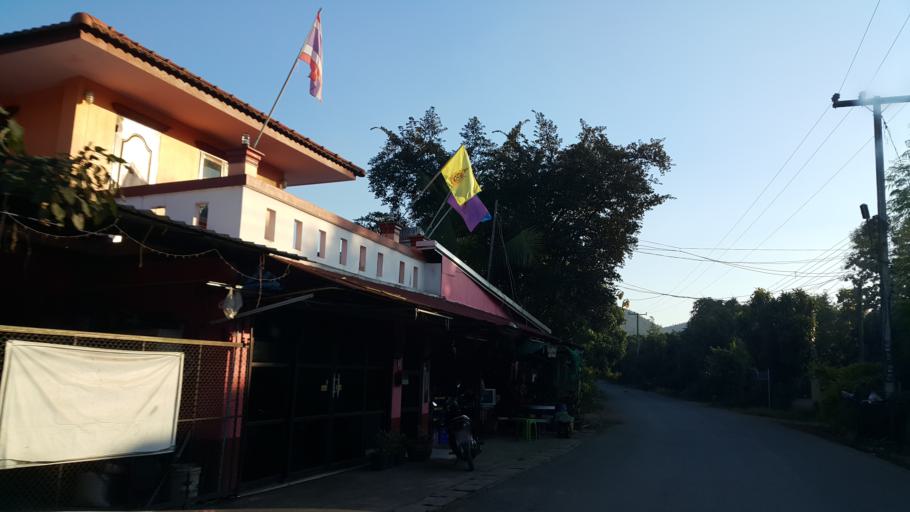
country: TH
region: Chiang Mai
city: Mae On
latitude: 18.7297
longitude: 99.2260
